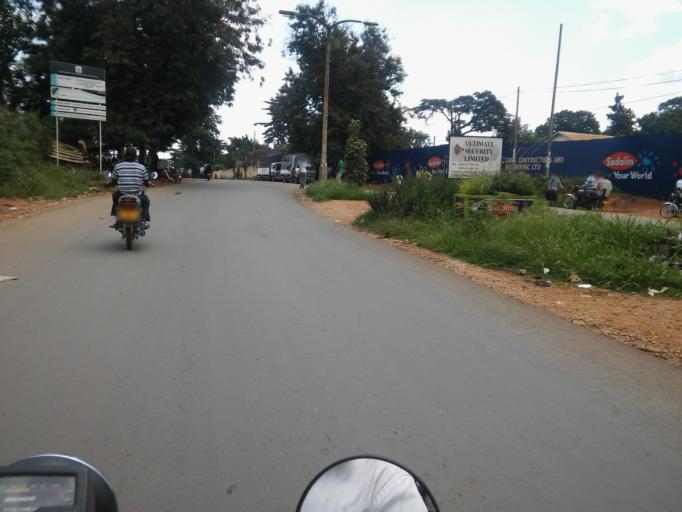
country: UG
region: Eastern Region
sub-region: Mbale District
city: Mbale
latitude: 1.0716
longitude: 34.1744
